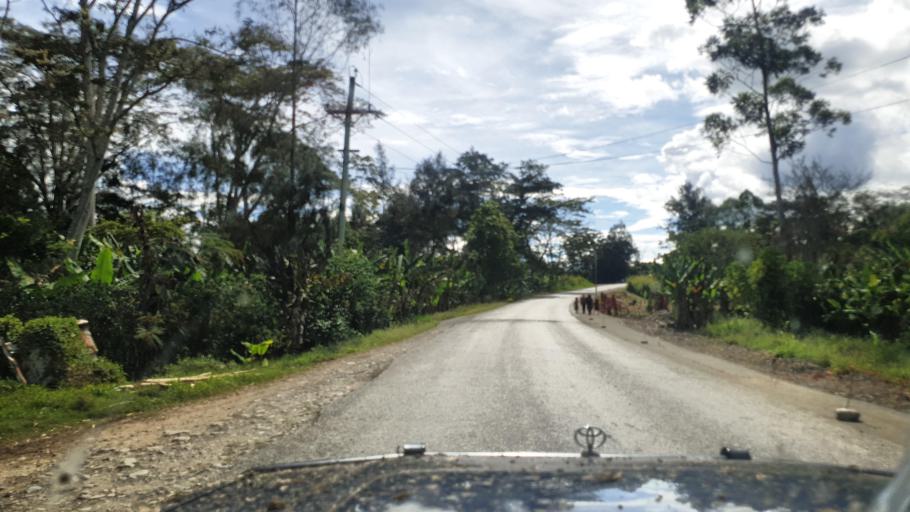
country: PG
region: Jiwaka
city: Minj
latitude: -5.8842
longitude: 144.7249
